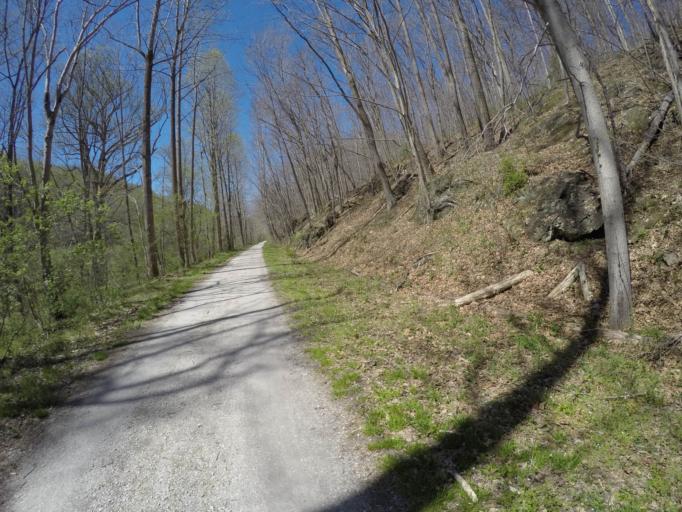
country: US
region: Maryland
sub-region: Baltimore County
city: Hunt Valley
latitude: 39.5948
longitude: -76.6223
